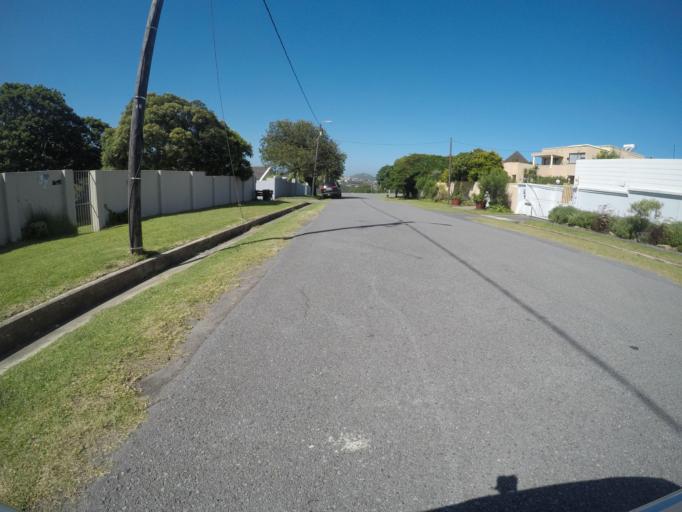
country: ZA
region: Eastern Cape
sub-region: Buffalo City Metropolitan Municipality
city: East London
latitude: -32.9856
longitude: 27.9439
